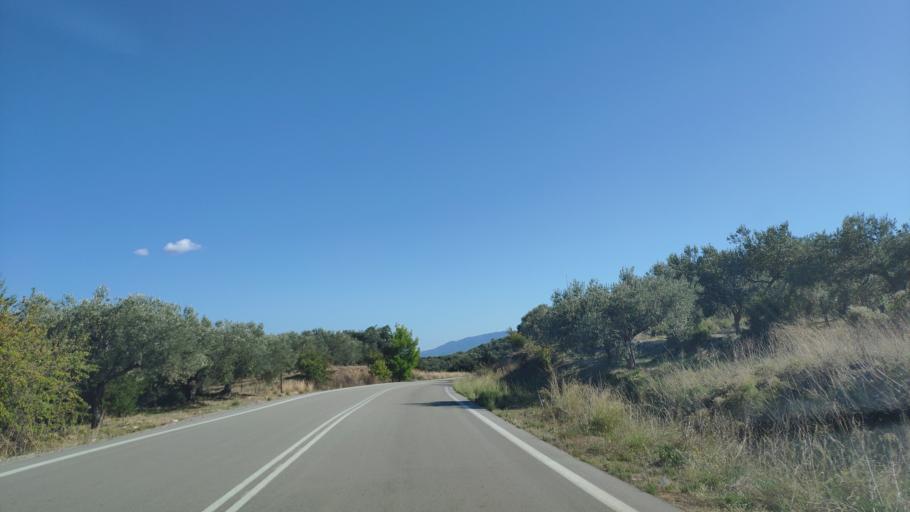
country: GR
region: Peloponnese
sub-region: Nomos Argolidos
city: Palaia Epidavros
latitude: 37.5754
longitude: 23.2467
